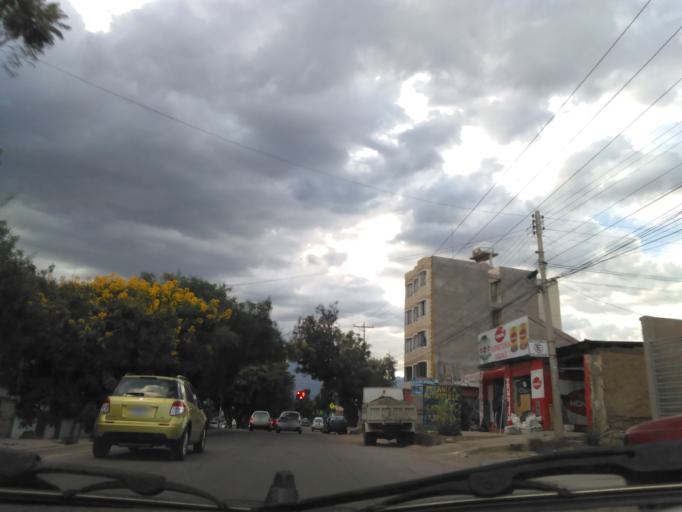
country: BO
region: Cochabamba
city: Cochabamba
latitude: -17.3645
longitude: -66.1637
